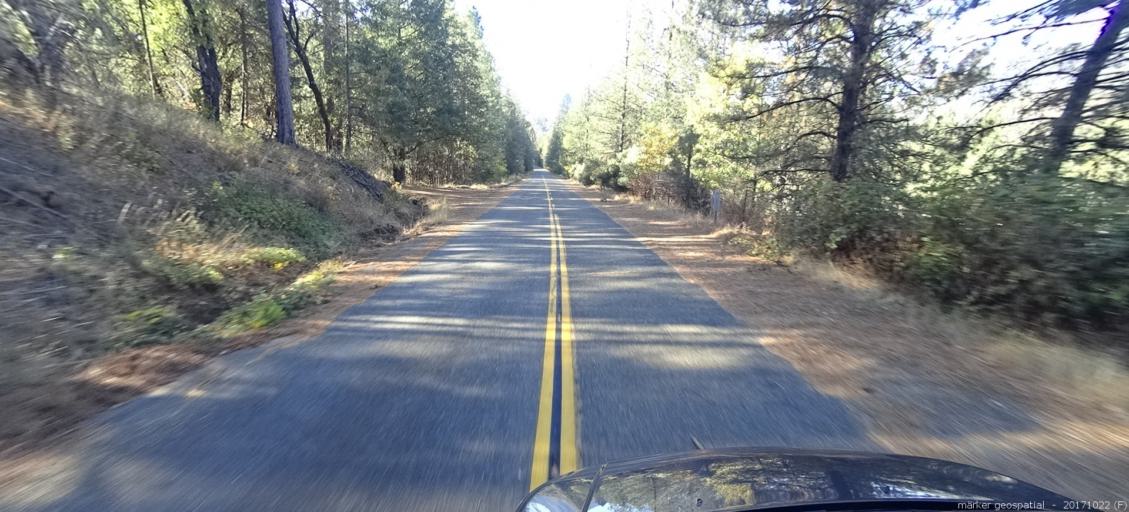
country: US
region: California
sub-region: Shasta County
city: Shasta Lake
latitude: 40.8438
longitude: -122.3299
